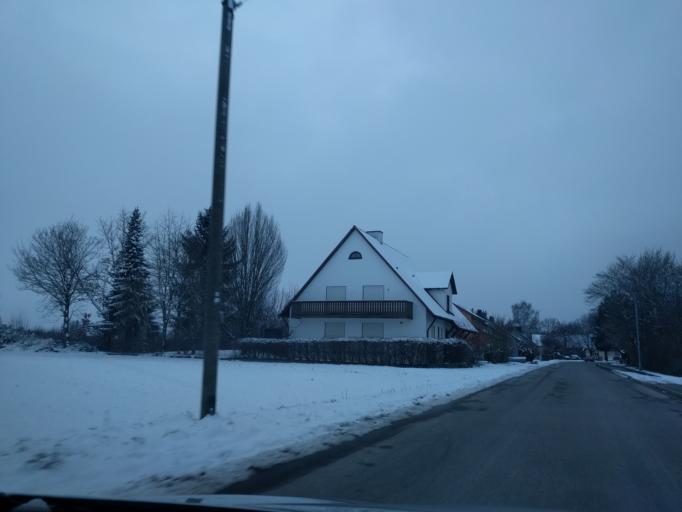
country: DE
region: Bavaria
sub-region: Swabia
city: Genderkingen
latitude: 48.7089
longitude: 10.8912
